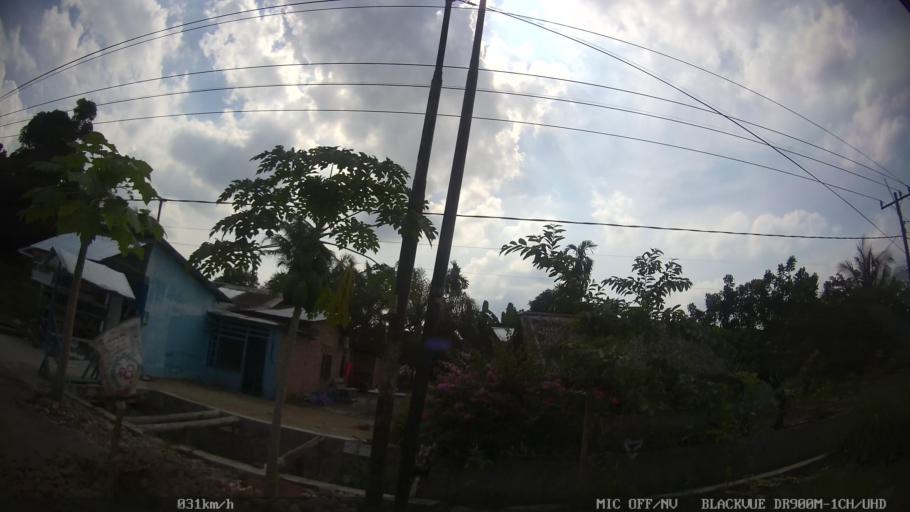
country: ID
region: North Sumatra
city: Binjai
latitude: 3.6446
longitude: 98.5179
